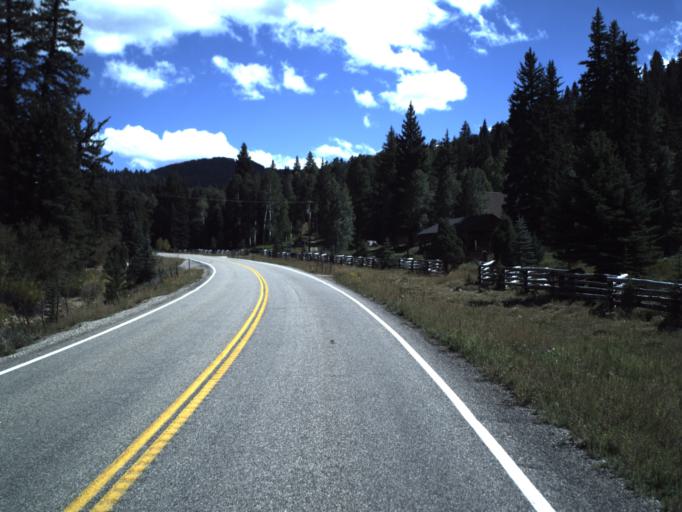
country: US
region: Utah
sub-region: Iron County
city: Cedar City
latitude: 37.5976
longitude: -112.9284
